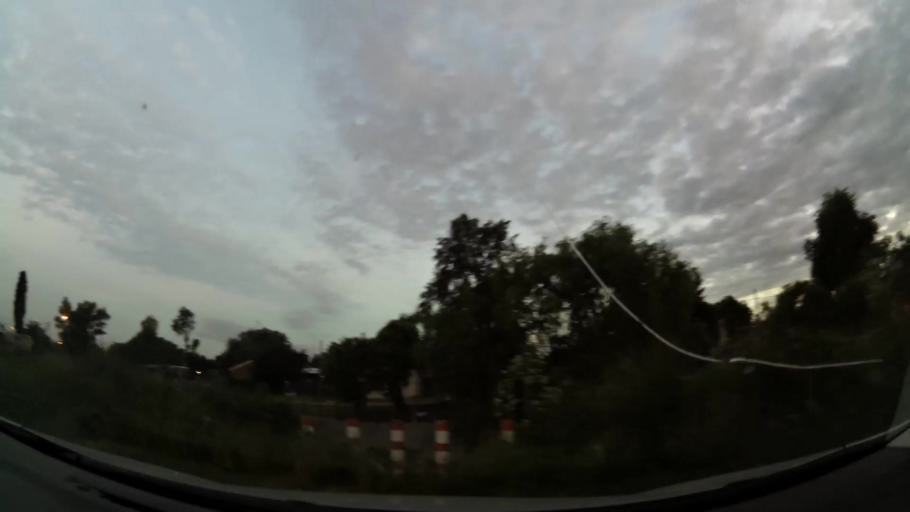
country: AR
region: Buenos Aires
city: Santa Catalina - Dique Lujan
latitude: -34.4170
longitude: -58.6902
